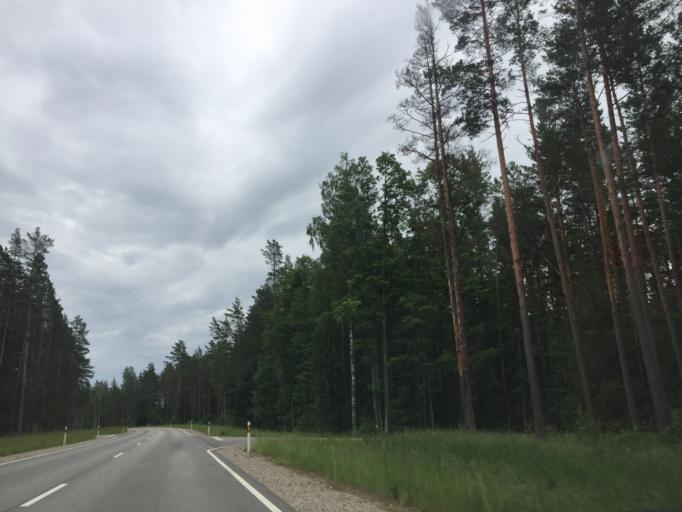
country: LV
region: Tukuma Rajons
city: Engure
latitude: 57.0824
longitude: 23.2431
